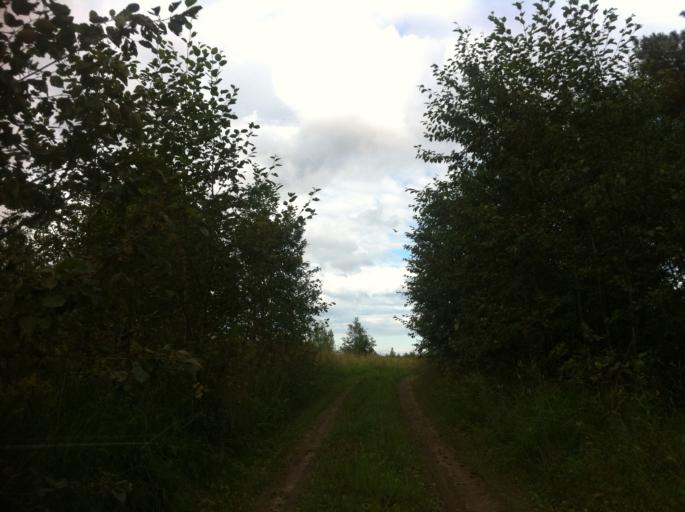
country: RU
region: Pskov
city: Izborsk
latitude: 57.8198
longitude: 27.9699
